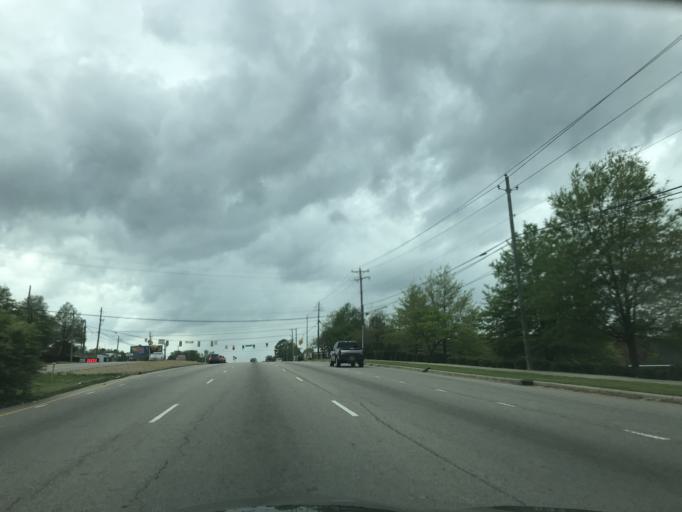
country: US
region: North Carolina
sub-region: Wake County
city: Knightdale
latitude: 35.7985
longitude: -78.5610
